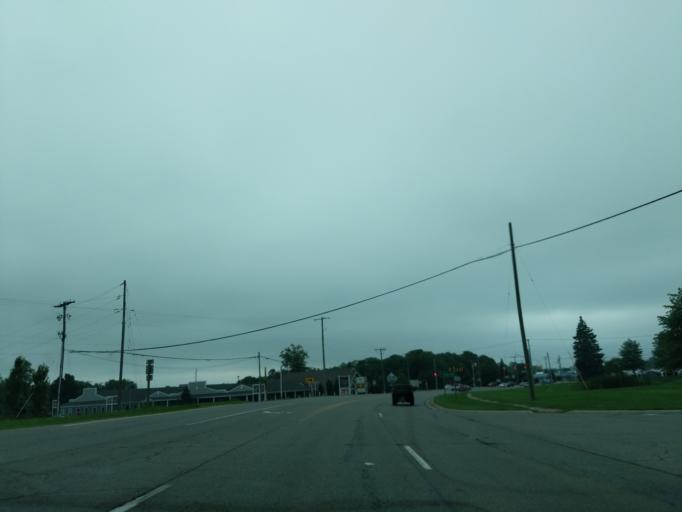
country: US
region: Michigan
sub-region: Branch County
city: Coldwater
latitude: 41.9347
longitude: -84.9593
